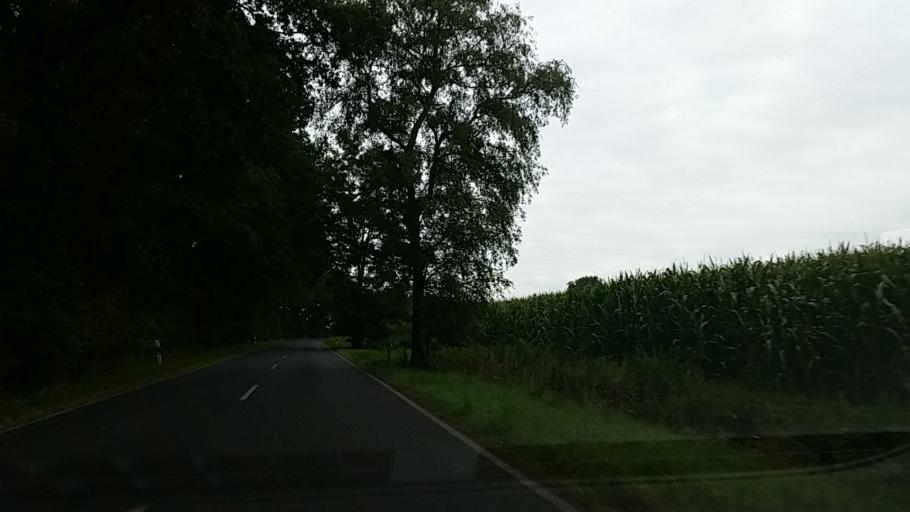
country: DE
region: Lower Saxony
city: Vollersode
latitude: 53.4024
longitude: 8.9217
